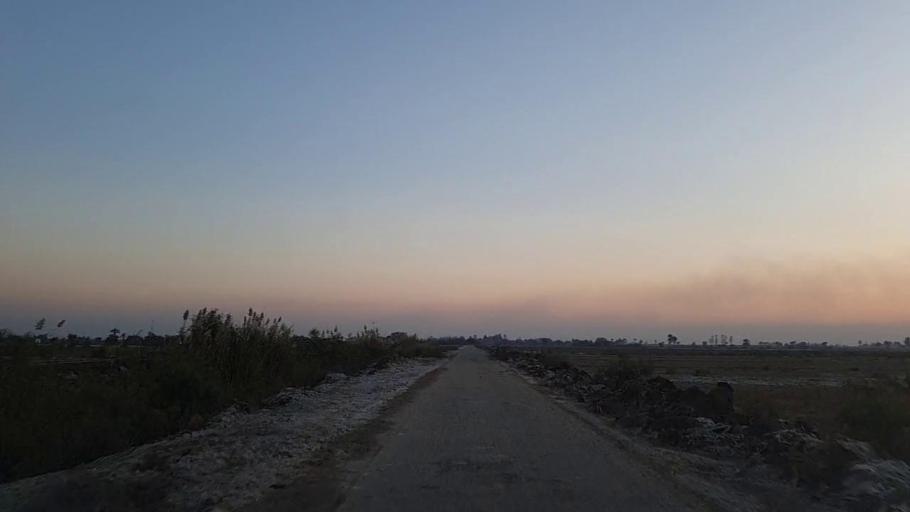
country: PK
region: Sindh
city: Bandhi
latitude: 26.5922
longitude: 68.3360
